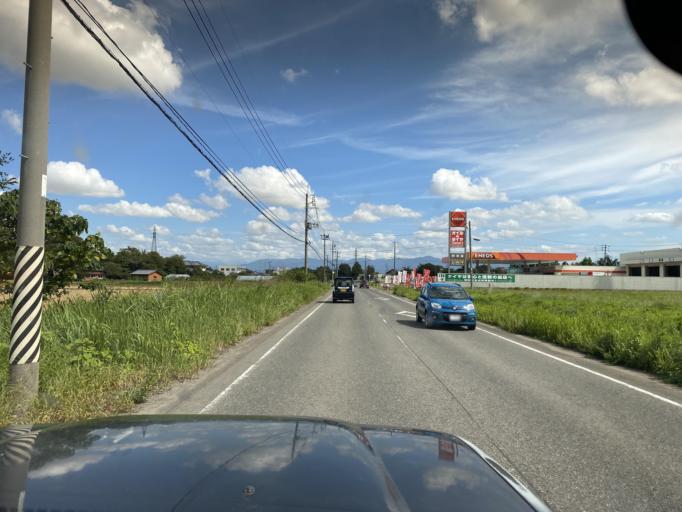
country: JP
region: Niigata
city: Niitsu-honcho
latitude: 37.8151
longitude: 139.1105
